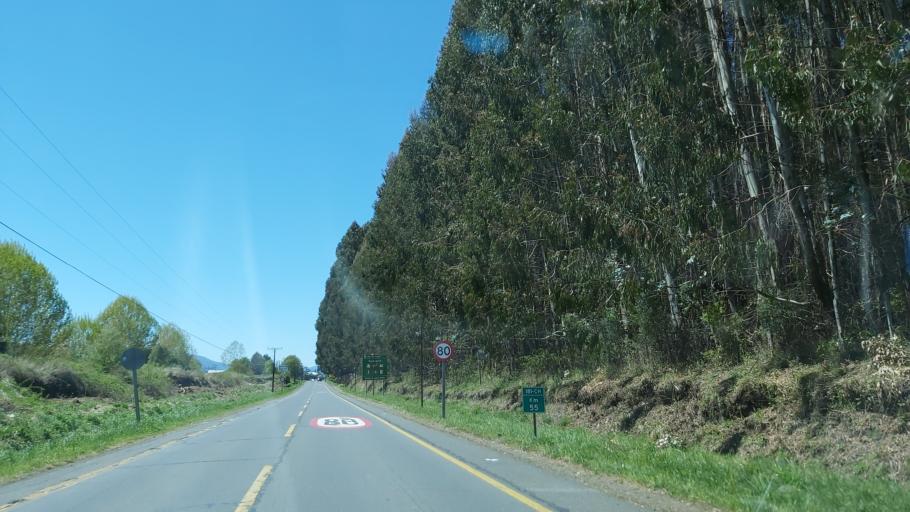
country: CL
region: Araucania
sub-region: Provincia de Cautin
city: Vilcun
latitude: -38.4336
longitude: -71.9072
